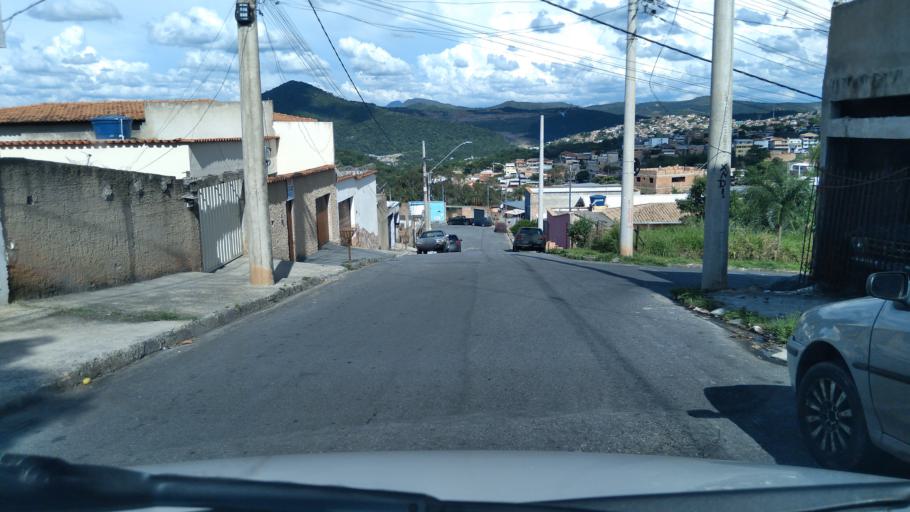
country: BR
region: Minas Gerais
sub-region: Belo Horizonte
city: Belo Horizonte
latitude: -19.8566
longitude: -43.8801
